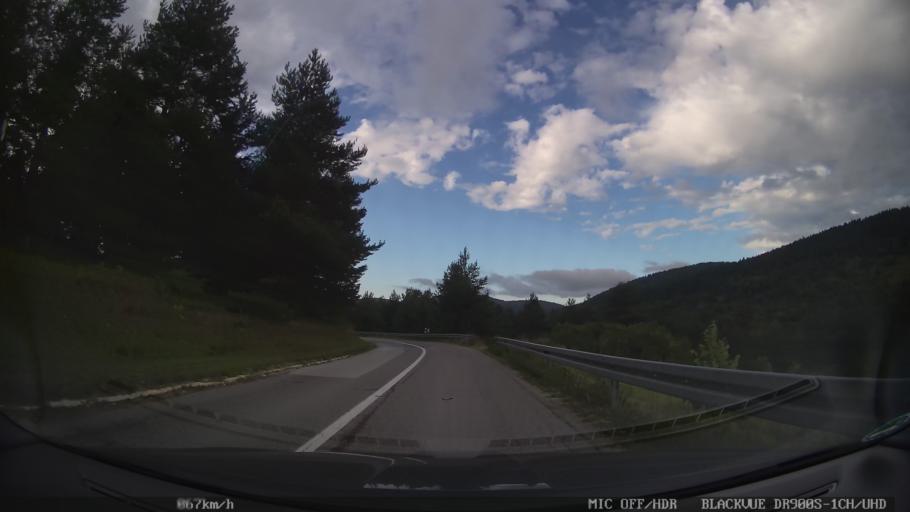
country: HR
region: Karlovacka
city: Plaski
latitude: 44.9920
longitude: 15.4682
